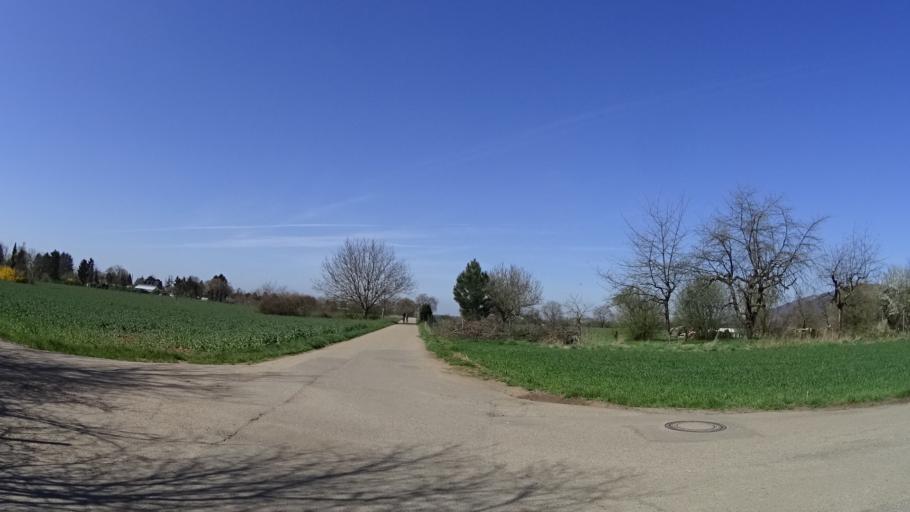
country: DE
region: Baden-Wuerttemberg
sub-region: Karlsruhe Region
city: Dossenheim
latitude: 49.4294
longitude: 8.6581
